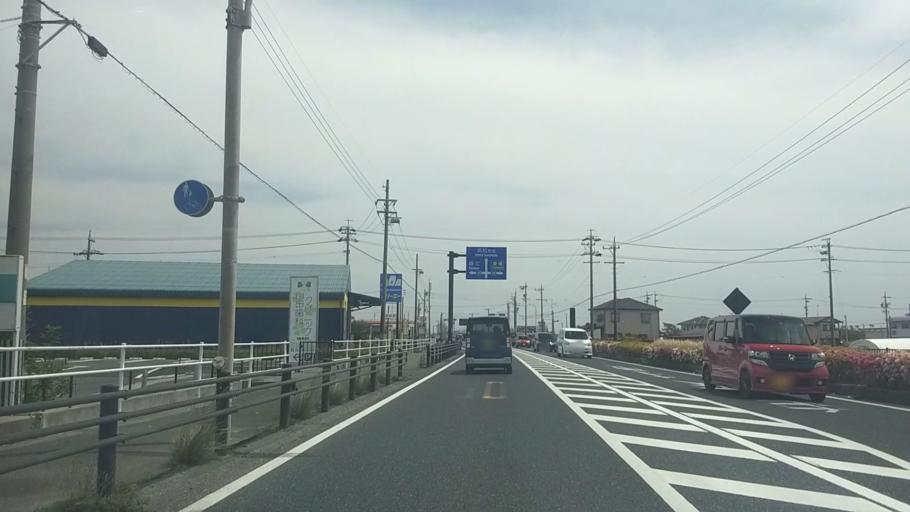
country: JP
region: Shizuoka
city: Kosai-shi
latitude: 34.6809
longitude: 137.6288
